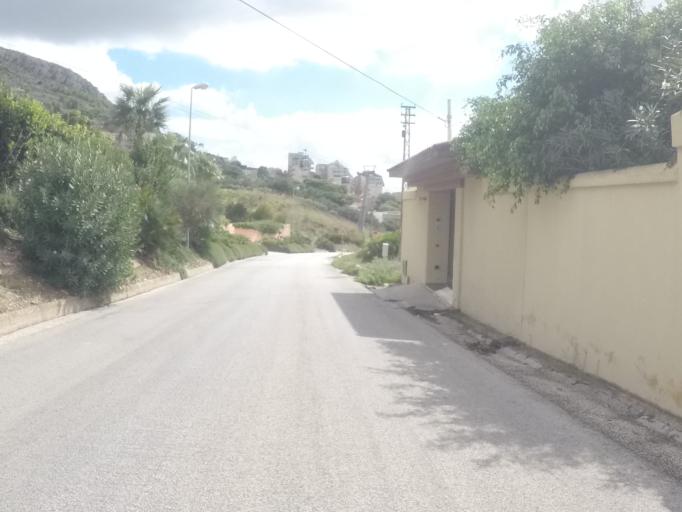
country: IT
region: Sicily
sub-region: Trapani
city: Casa Santa
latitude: 38.0261
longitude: 12.5523
